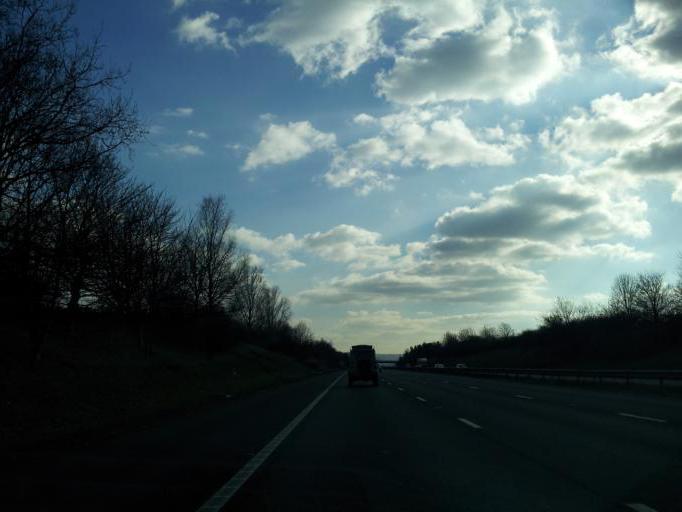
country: GB
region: England
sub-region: Somerset
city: Creech Saint Michael
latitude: 51.0523
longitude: -3.0259
